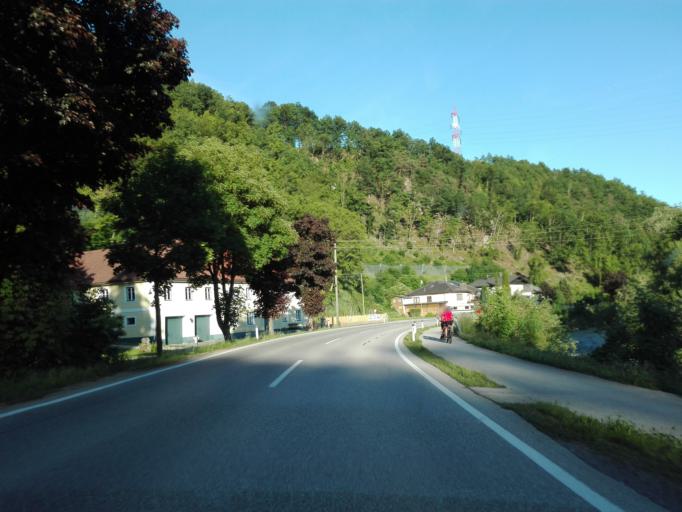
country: AT
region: Upper Austria
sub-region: Politischer Bezirk Rohrbach
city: Kleinzell im Muehlkreis
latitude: 48.3773
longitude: 13.9556
